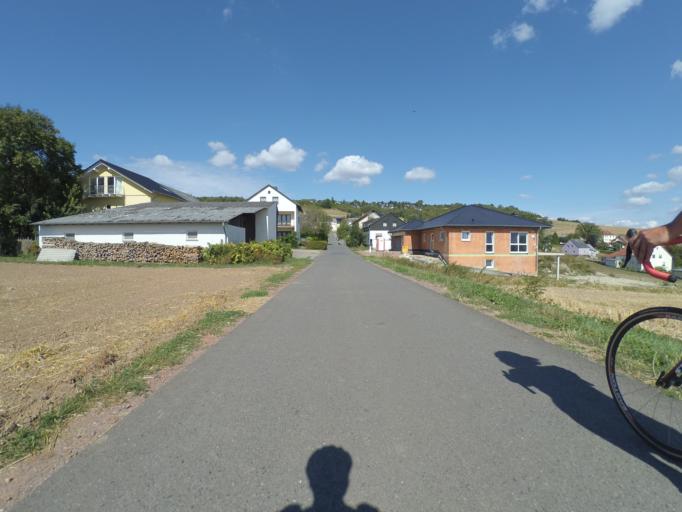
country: DE
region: Rheinland-Pfalz
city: Merzkirchen
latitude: 49.5938
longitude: 6.5084
